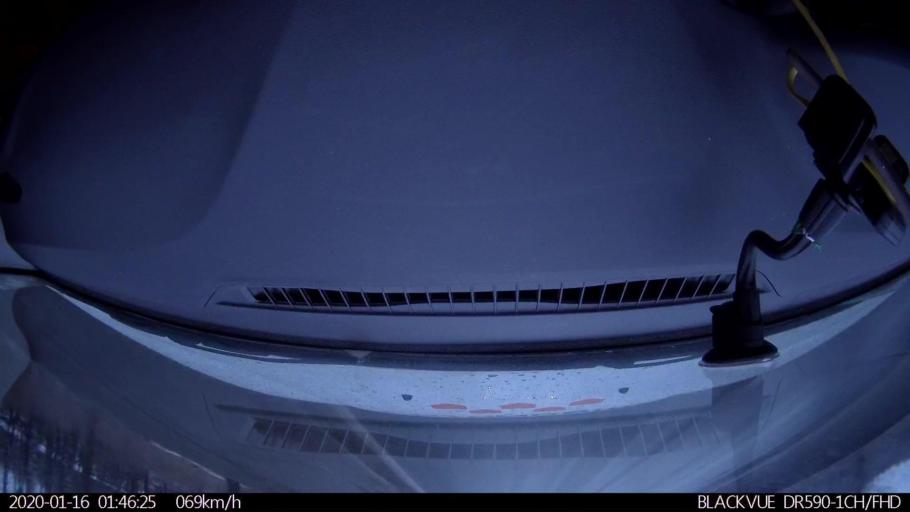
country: RU
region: Nizjnij Novgorod
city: Gorbatovka
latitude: 56.3103
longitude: 43.7819
